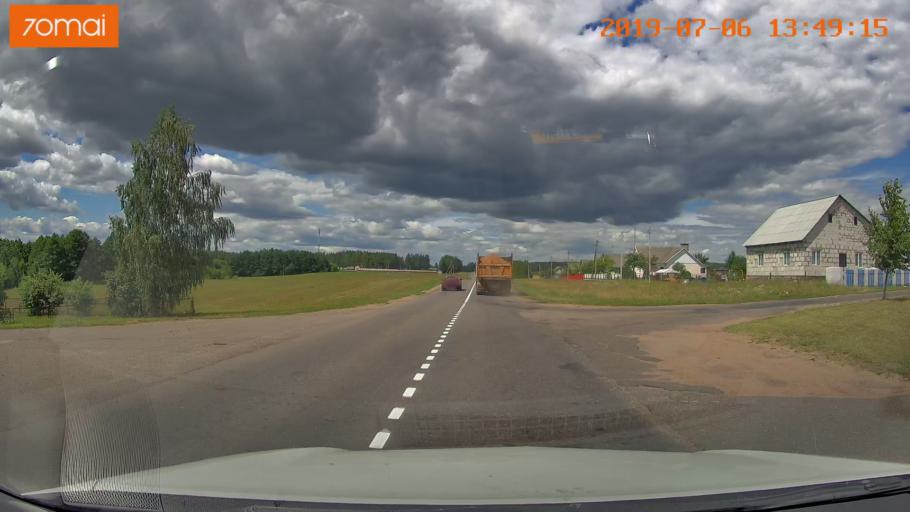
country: BY
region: Minsk
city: Ivyanyets
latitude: 53.6930
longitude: 26.8530
